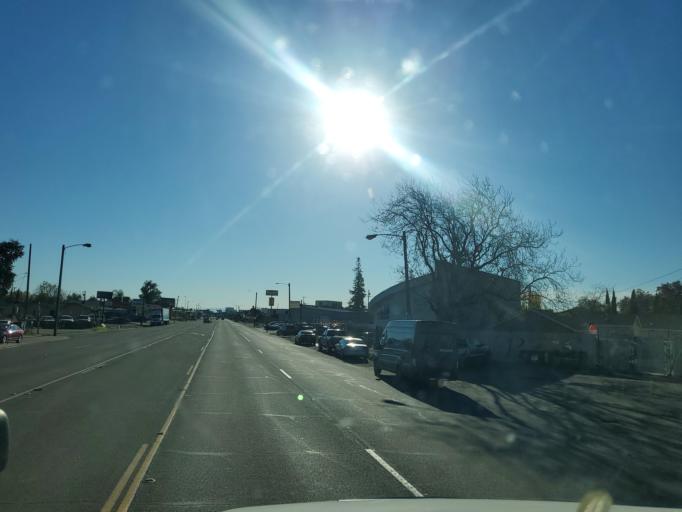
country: US
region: California
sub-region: San Joaquin County
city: August
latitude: 37.9863
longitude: -121.2696
